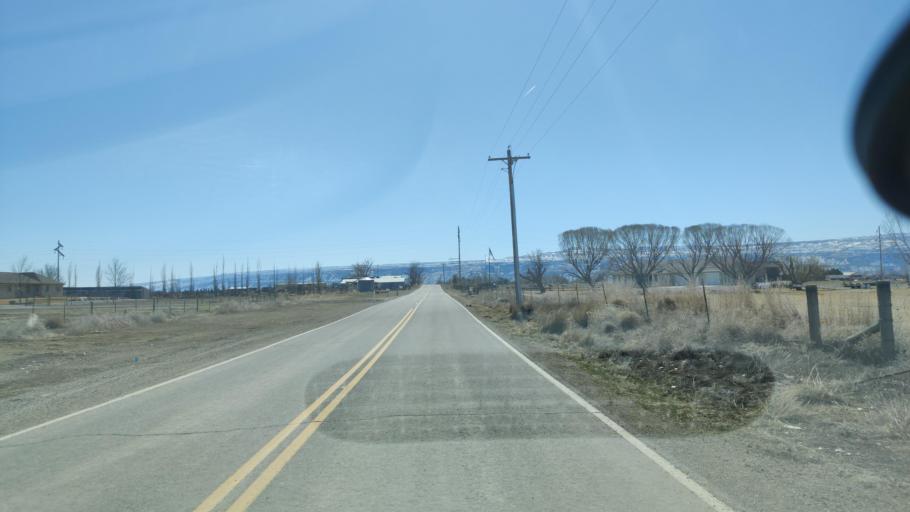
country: US
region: Colorado
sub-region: Mesa County
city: Fruita
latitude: 39.1913
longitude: -108.7105
